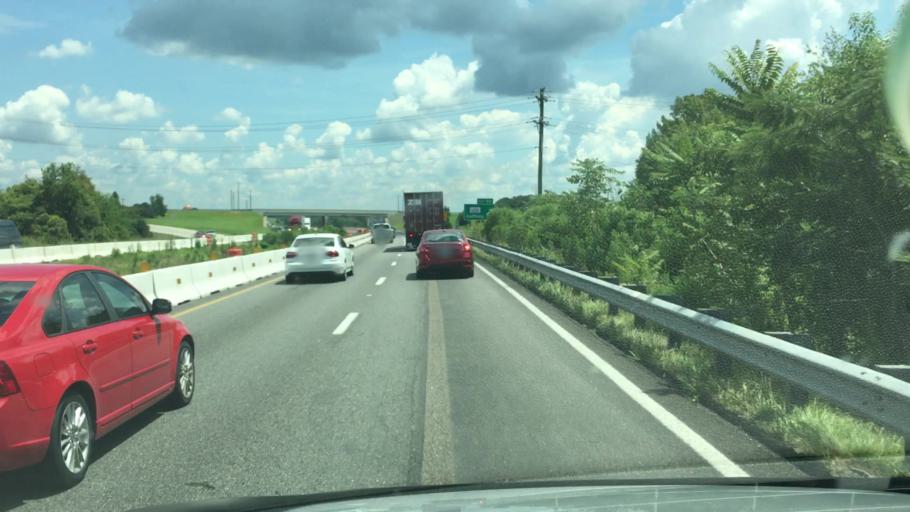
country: US
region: South Carolina
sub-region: Cherokee County
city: Gaffney
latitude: 35.0812
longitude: -81.7120
